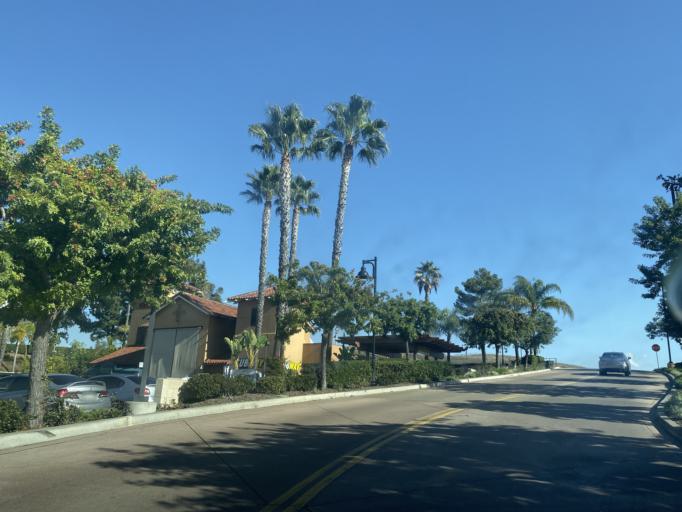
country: US
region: California
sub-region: Orange County
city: North Tustin
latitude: 33.7916
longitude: -117.7625
